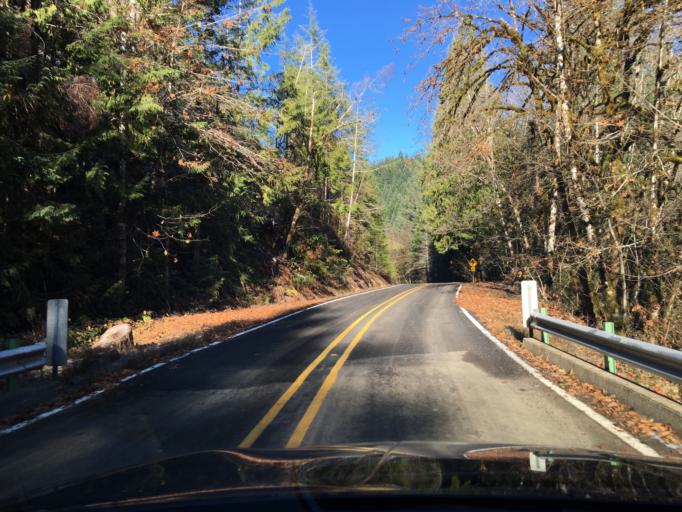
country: US
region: Oregon
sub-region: Douglas County
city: Roseburg
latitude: 43.3244
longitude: -123.5832
